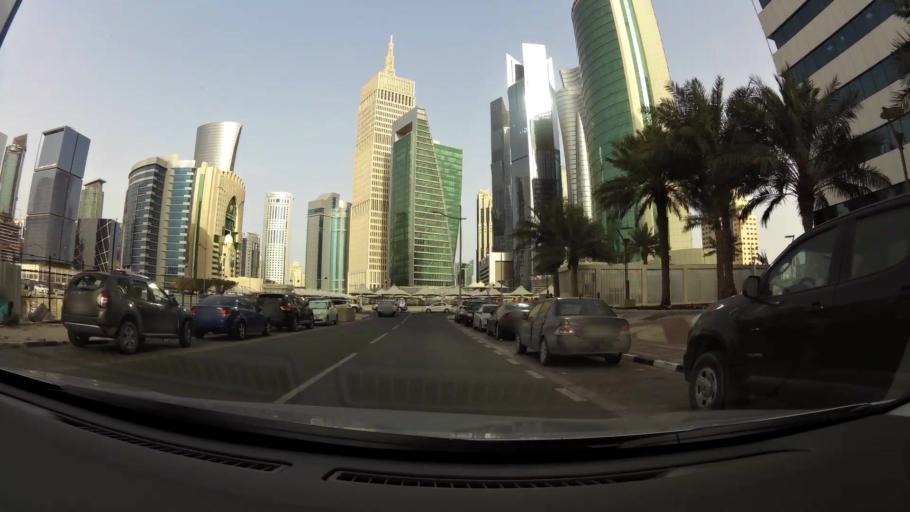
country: QA
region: Baladiyat ad Dawhah
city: Doha
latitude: 25.3192
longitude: 51.5224
